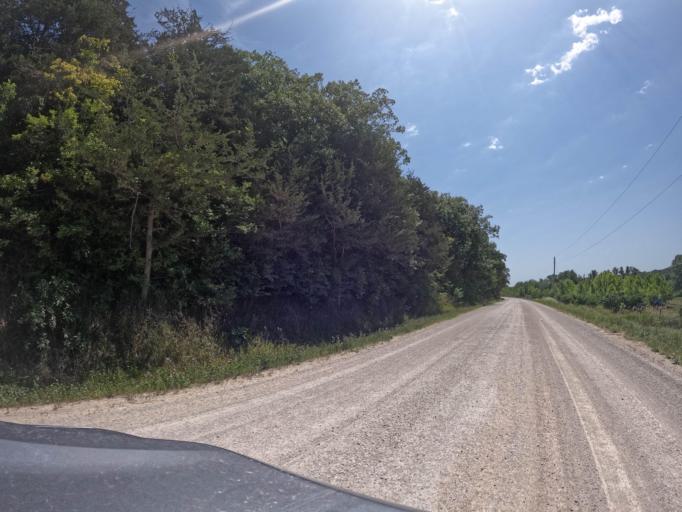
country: US
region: Iowa
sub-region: Henry County
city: Mount Pleasant
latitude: 40.8978
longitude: -91.5509
